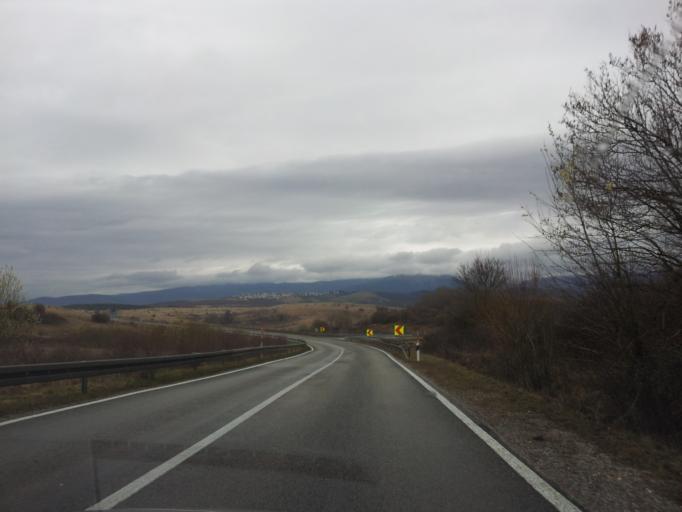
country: HR
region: Zadarska
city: Gracac
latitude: 44.4956
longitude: 15.7459
